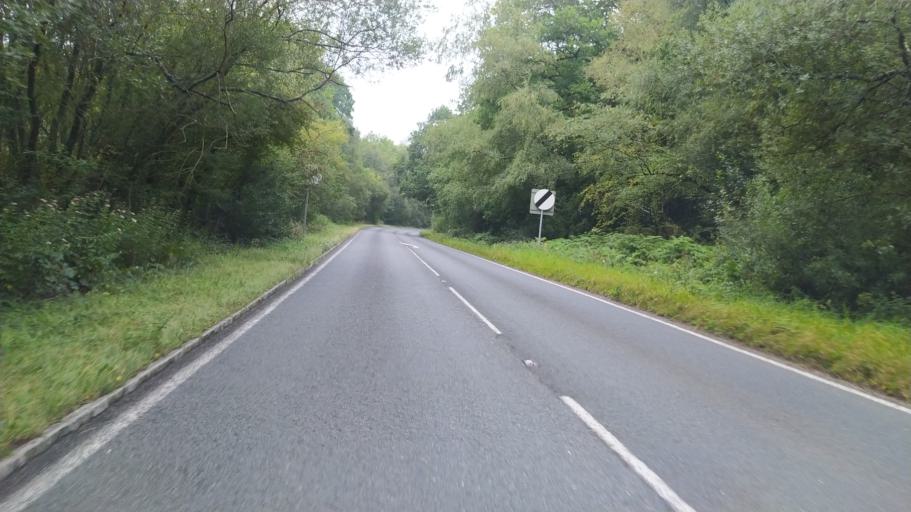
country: GB
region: England
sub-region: Hampshire
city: New Milton
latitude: 50.8019
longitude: -1.6734
